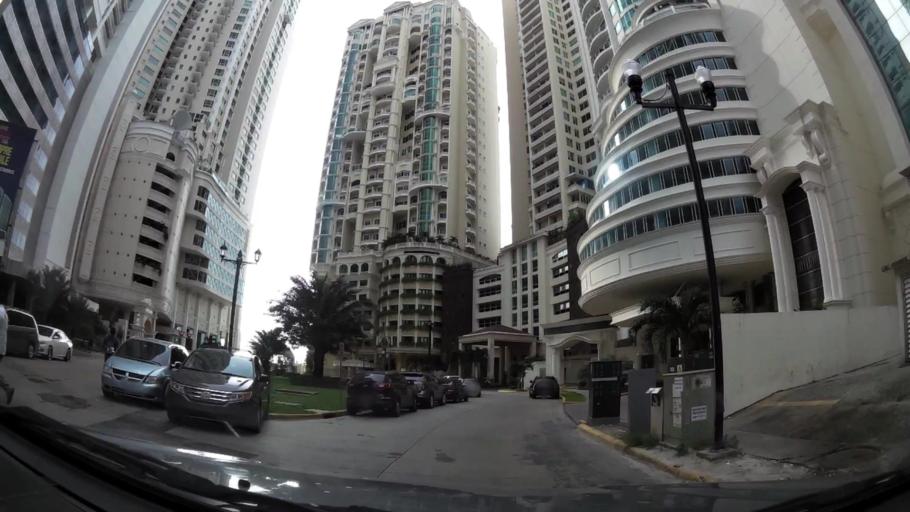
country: PA
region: Panama
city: Panama
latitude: 8.9749
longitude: -79.5075
